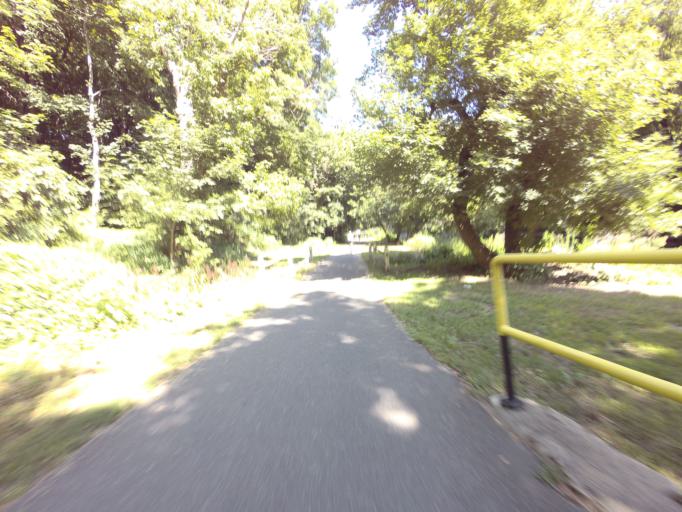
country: US
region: Pennsylvania
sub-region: Montgomery County
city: Bala-Cynwyd
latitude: 40.0167
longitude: -75.2050
